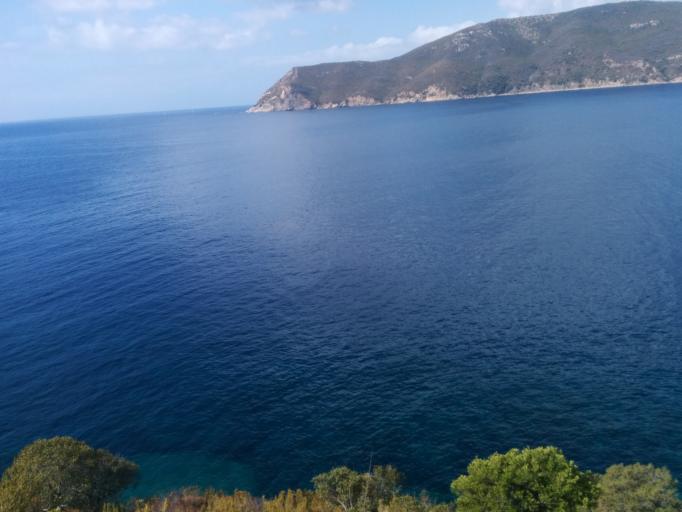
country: IT
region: Tuscany
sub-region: Provincia di Livorno
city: Capoliveri
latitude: 42.7473
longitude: 10.3150
